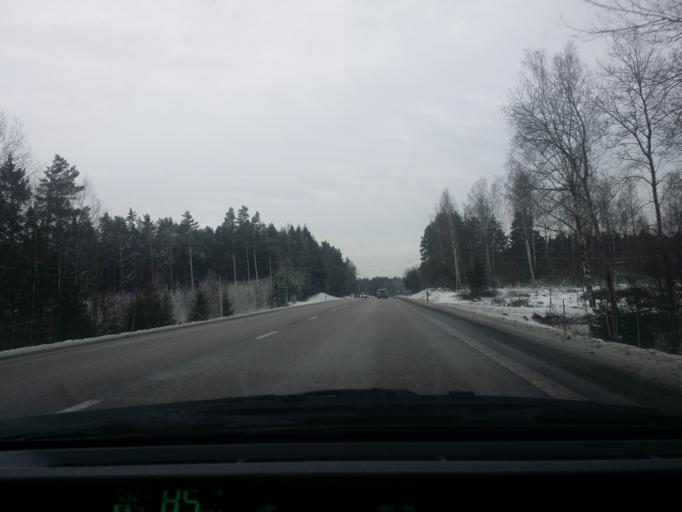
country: SE
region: Vaestra Goetaland
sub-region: Mariestads Kommun
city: Mariestad
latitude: 58.7188
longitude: 13.8815
